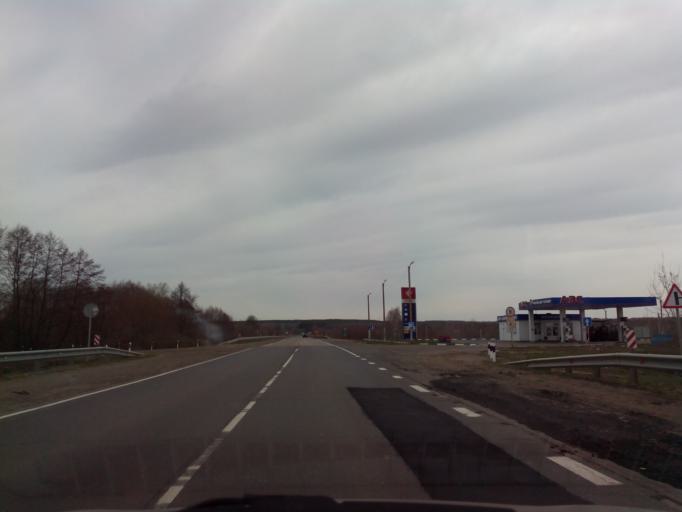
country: RU
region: Tambov
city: Znamenka
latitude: 52.5219
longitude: 41.3626
